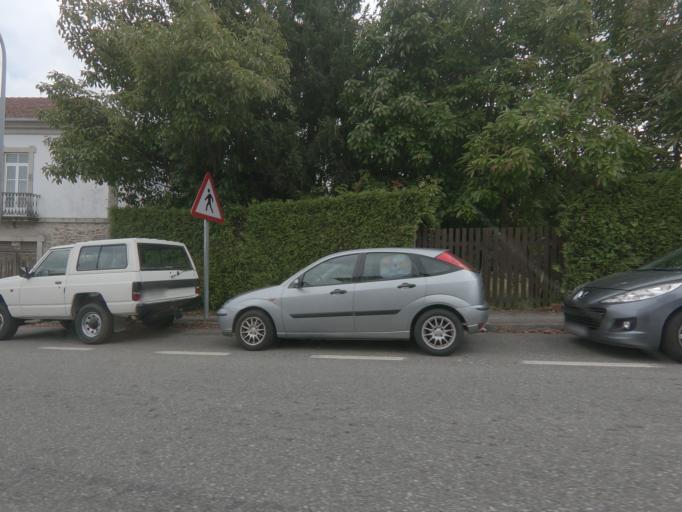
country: PT
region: Viana do Castelo
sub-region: Vila Nova de Cerveira
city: Vila Nova de Cerveira
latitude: 41.9471
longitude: -8.7759
